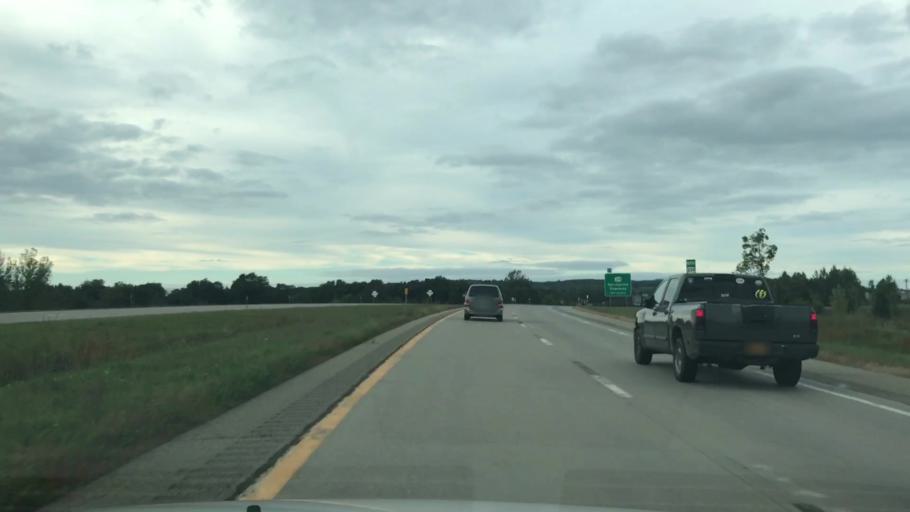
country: US
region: New York
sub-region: Erie County
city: Springville
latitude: 42.4970
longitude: -78.6973
